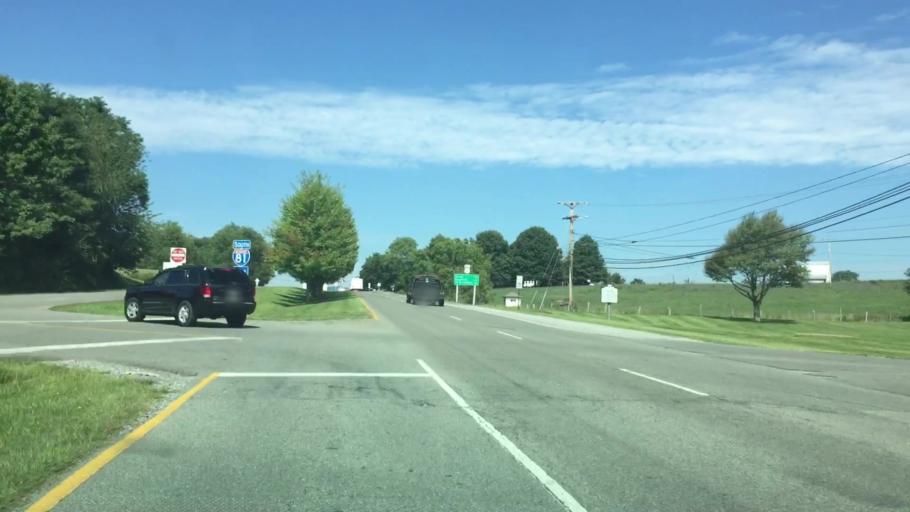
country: US
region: Virginia
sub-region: Wythe County
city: Wytheville
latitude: 36.9608
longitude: -81.1009
